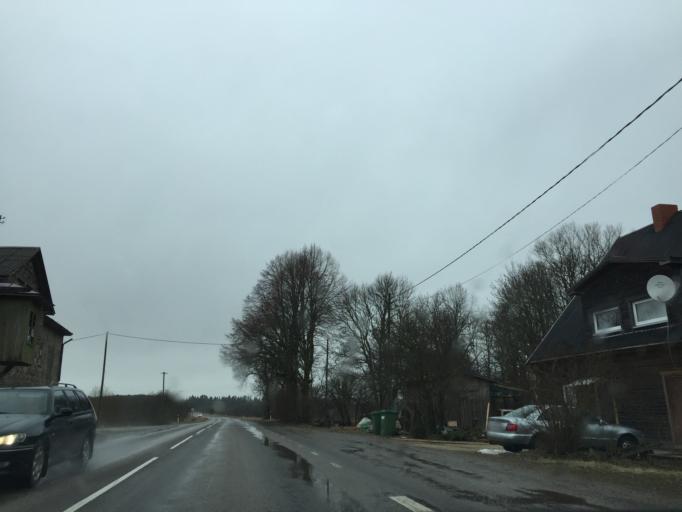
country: EE
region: Laeaene
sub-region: Ridala Parish
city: Uuemoisa
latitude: 58.8675
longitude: 23.6216
